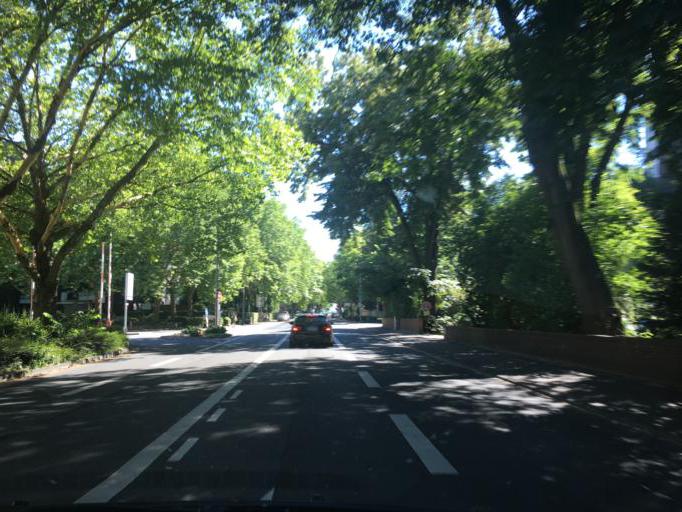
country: DE
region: North Rhine-Westphalia
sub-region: Regierungsbezirk Koln
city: Frechen
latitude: 50.9372
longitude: 6.8334
